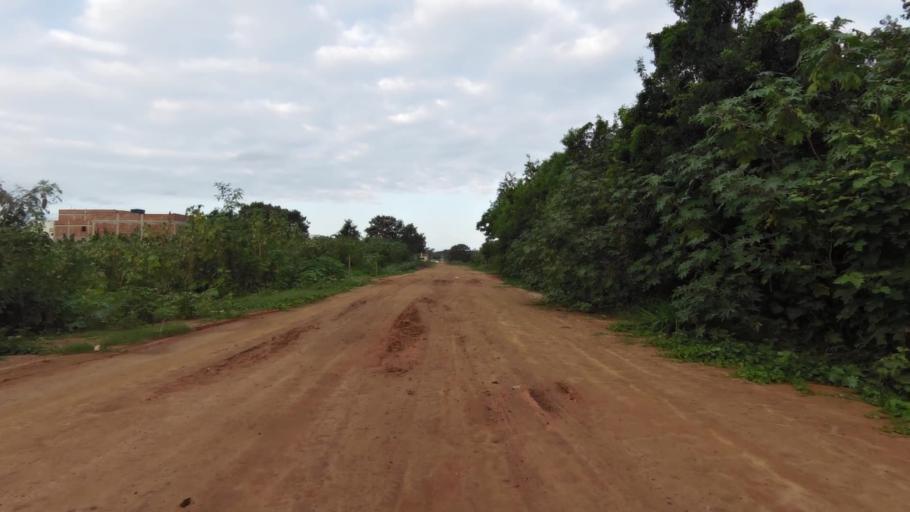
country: BR
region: Espirito Santo
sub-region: Piuma
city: Piuma
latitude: -20.8041
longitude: -40.6468
